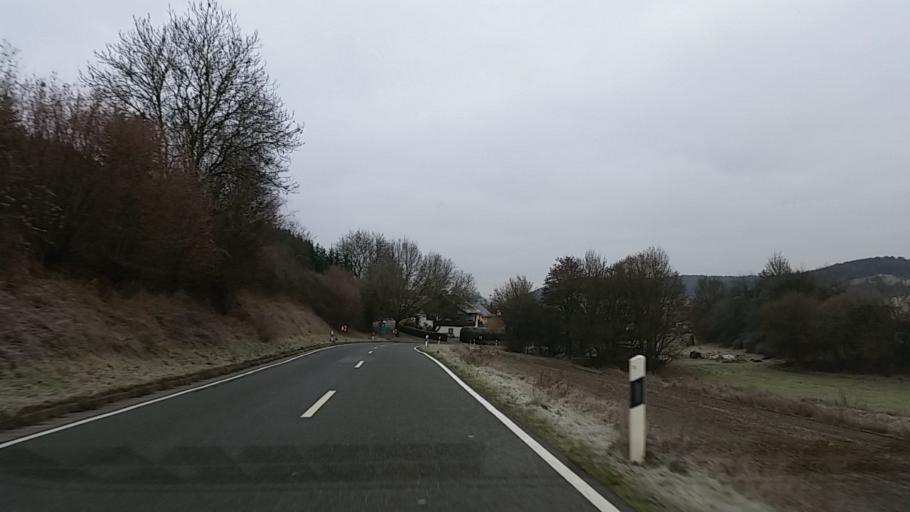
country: DE
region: Bavaria
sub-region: Regierungsbezirk Unterfranken
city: Fuchsstadt
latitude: 50.0998
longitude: 9.9277
